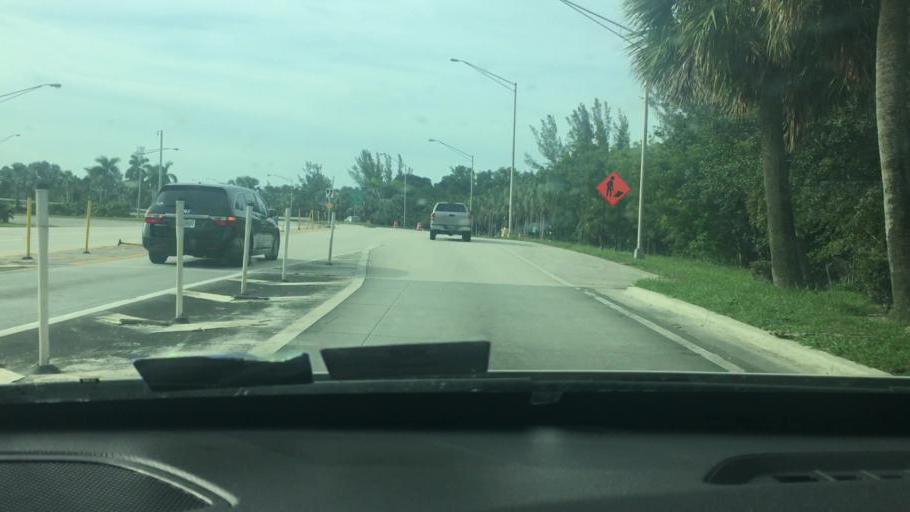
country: US
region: Florida
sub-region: Palm Beach County
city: Plantation Mobile Home Park
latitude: 26.7090
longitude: -80.1369
